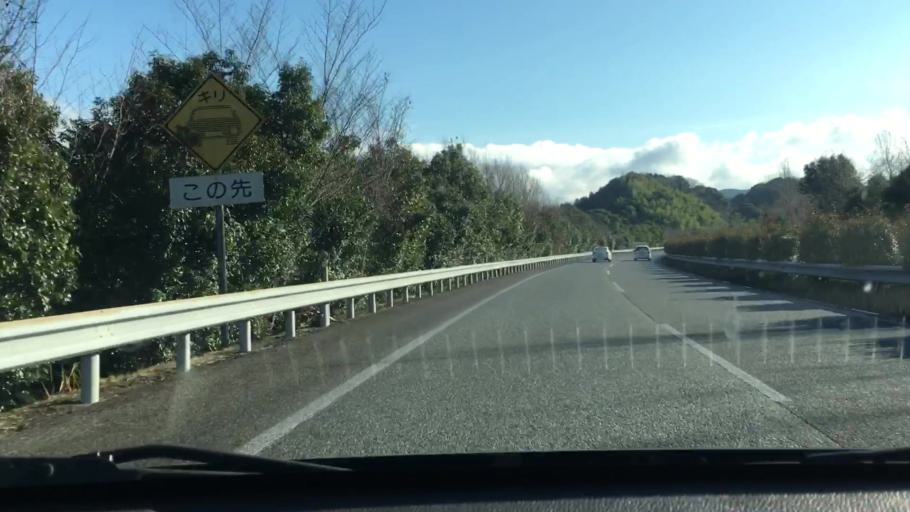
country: JP
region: Kumamoto
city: Hitoyoshi
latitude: 32.1969
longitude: 130.7776
